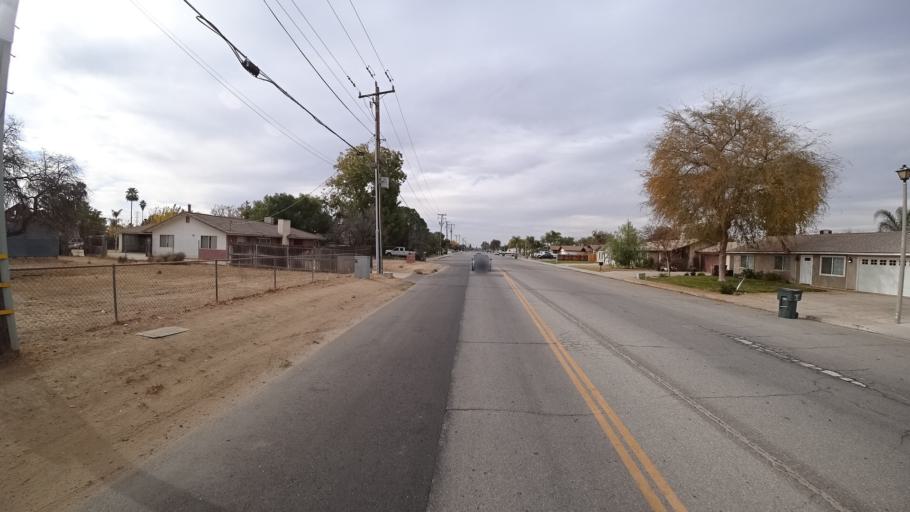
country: US
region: California
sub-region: Kern County
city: Greenacres
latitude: 35.3907
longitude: -119.1199
